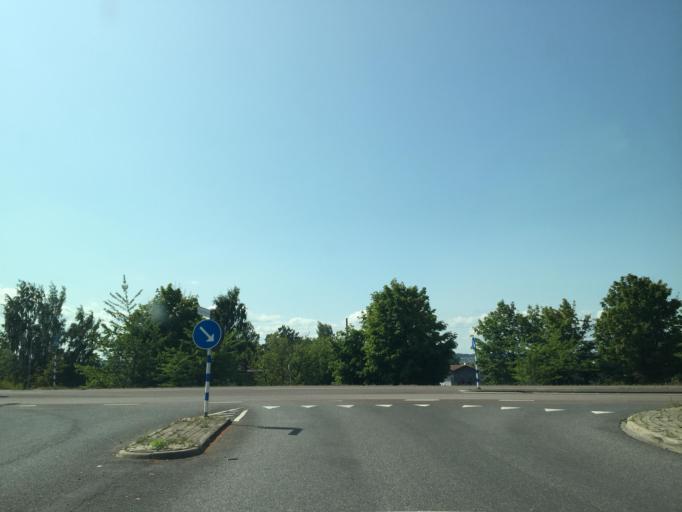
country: SE
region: Joenkoeping
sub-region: Jonkopings Kommun
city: Jonkoping
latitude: 57.7752
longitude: 14.1993
